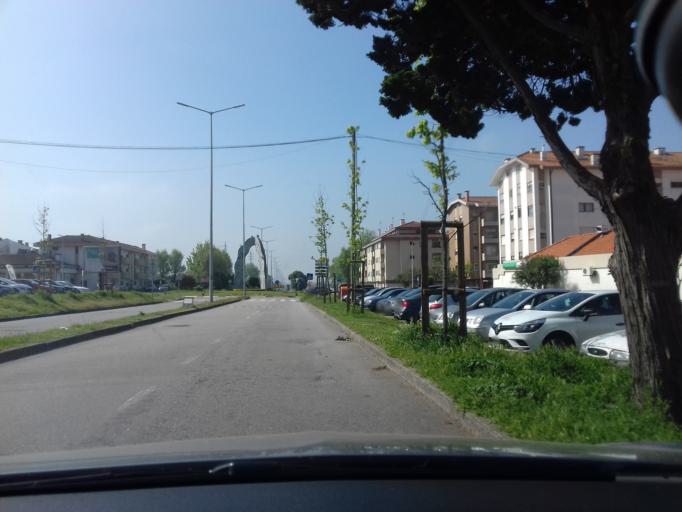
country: PT
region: Aveiro
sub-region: Espinho
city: Espinho
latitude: 41.0048
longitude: -8.6343
